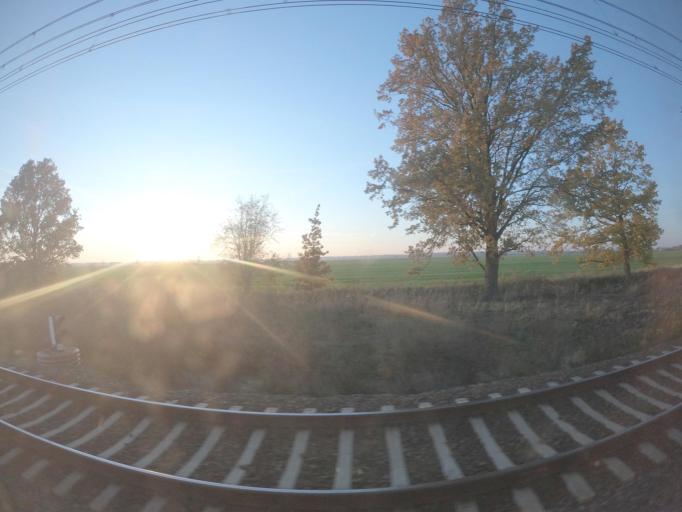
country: PL
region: Lubusz
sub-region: Powiat slubicki
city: Gorzyca
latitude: 52.5249
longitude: 14.6505
